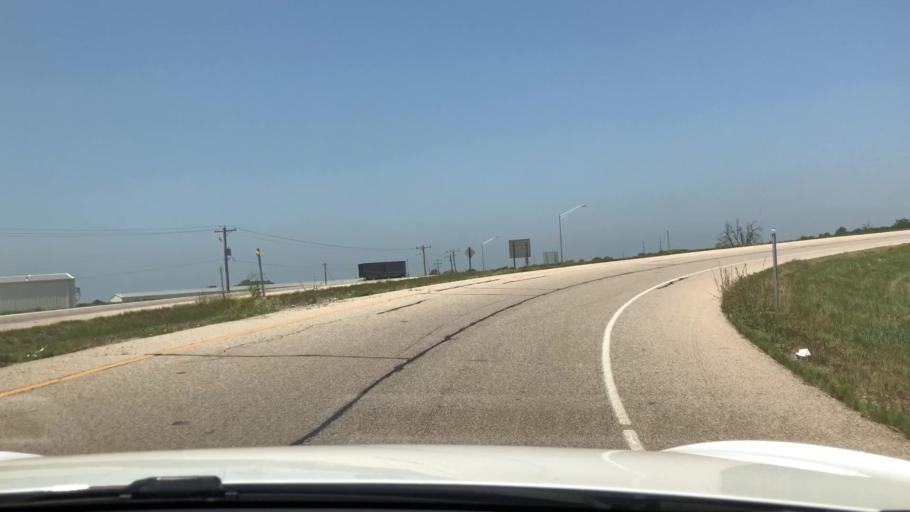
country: US
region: Illinois
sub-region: McLean County
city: Bloomington
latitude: 40.4347
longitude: -88.9919
